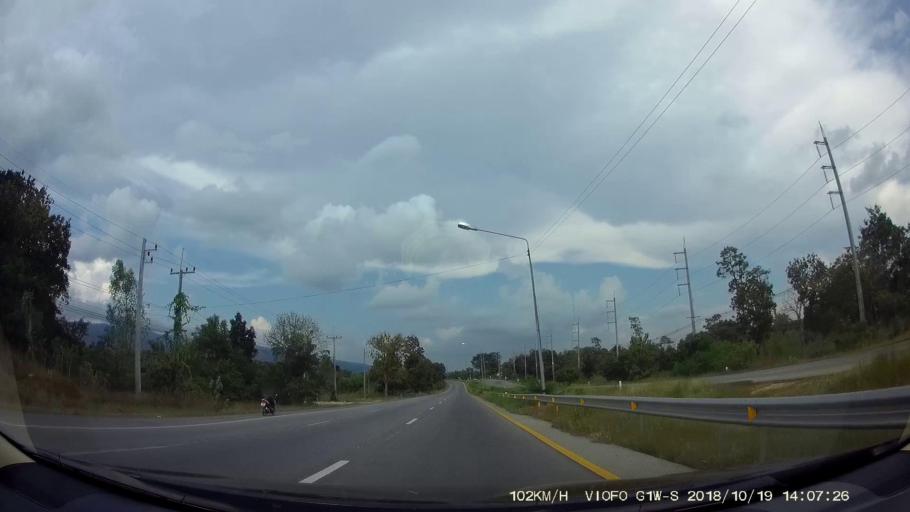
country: TH
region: Chaiyaphum
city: Chaiyaphum
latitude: 15.8937
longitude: 102.1170
